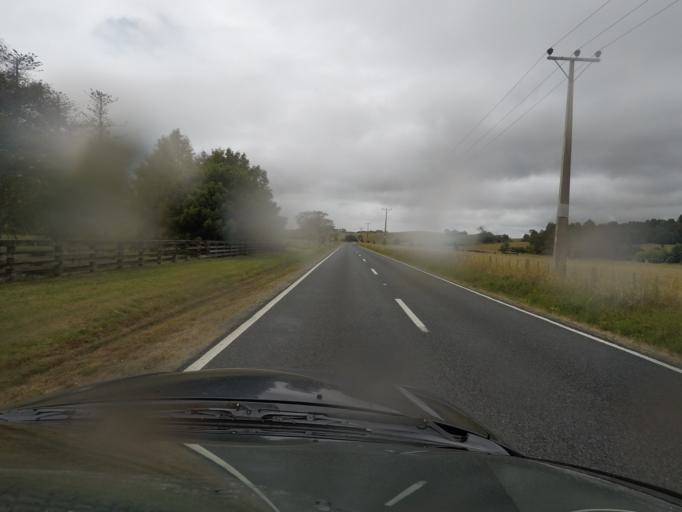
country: NZ
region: Auckland
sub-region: Auckland
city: Warkworth
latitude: -36.3390
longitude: 174.7030
